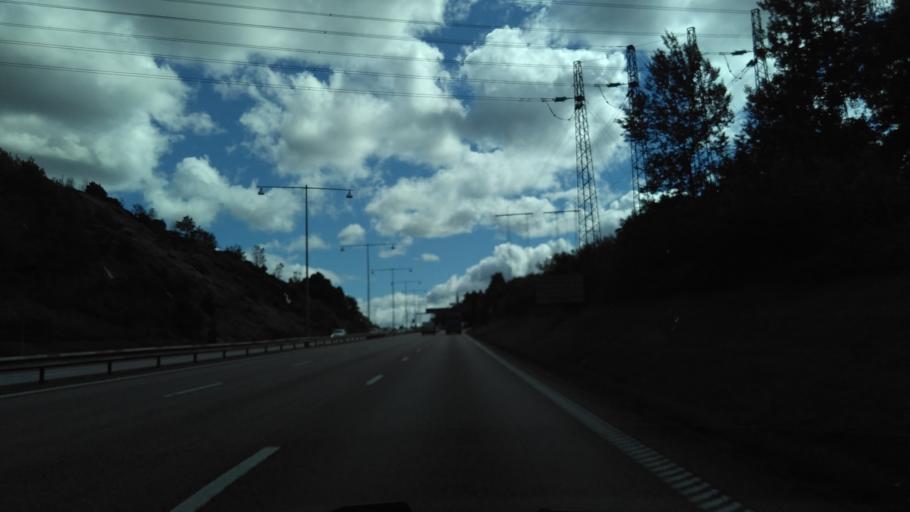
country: SE
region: Vaestra Goetaland
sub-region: Molndal
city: Moelndal
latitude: 57.6809
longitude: 12.0189
